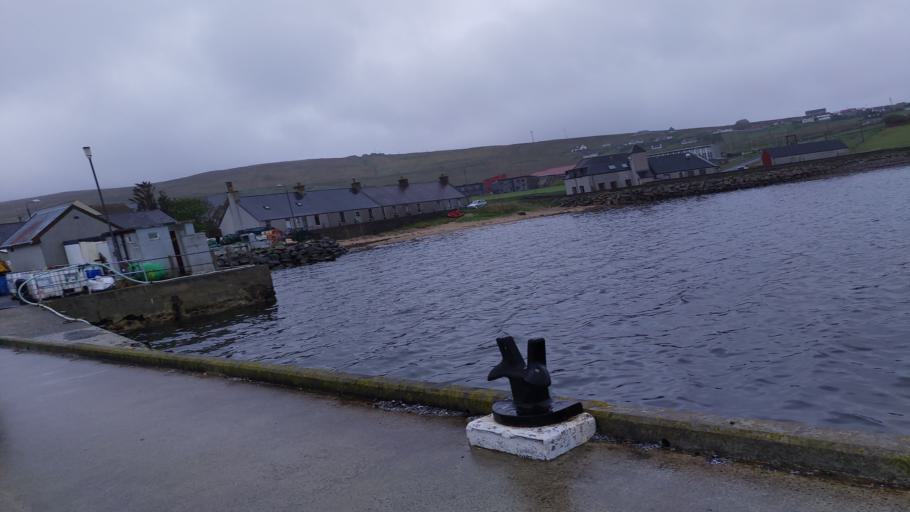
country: GB
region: Scotland
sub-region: Shetland Islands
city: Shetland
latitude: 60.5983
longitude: -1.0588
